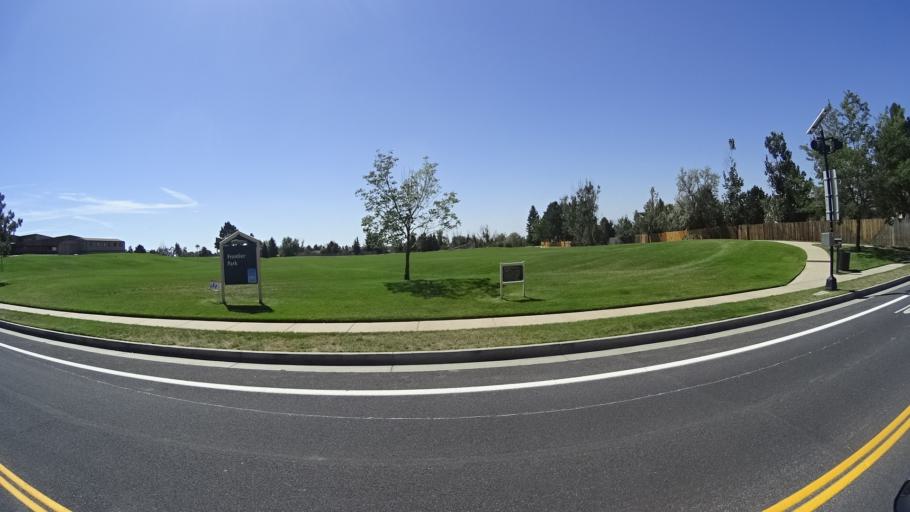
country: US
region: Colorado
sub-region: El Paso County
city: Black Forest
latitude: 38.9477
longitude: -104.7574
